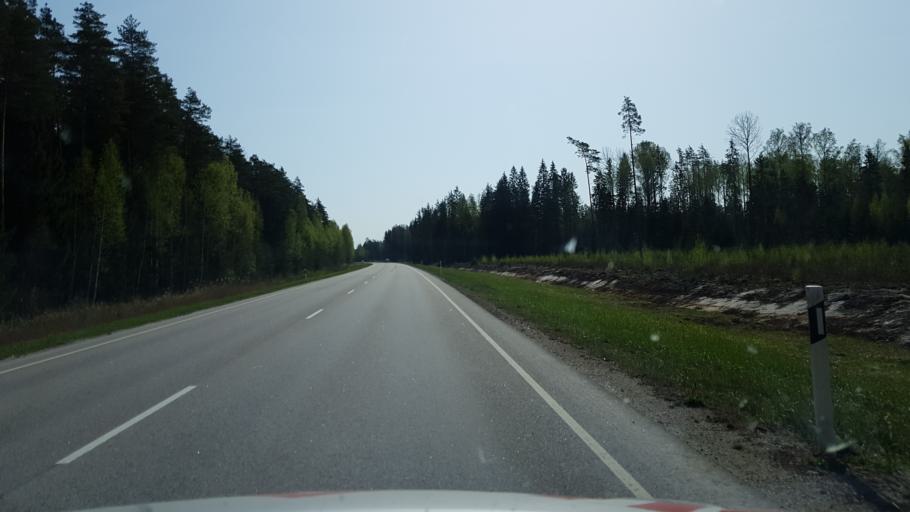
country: EE
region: Paernumaa
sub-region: Saarde vald
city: Kilingi-Nomme
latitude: 58.1652
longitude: 24.8300
